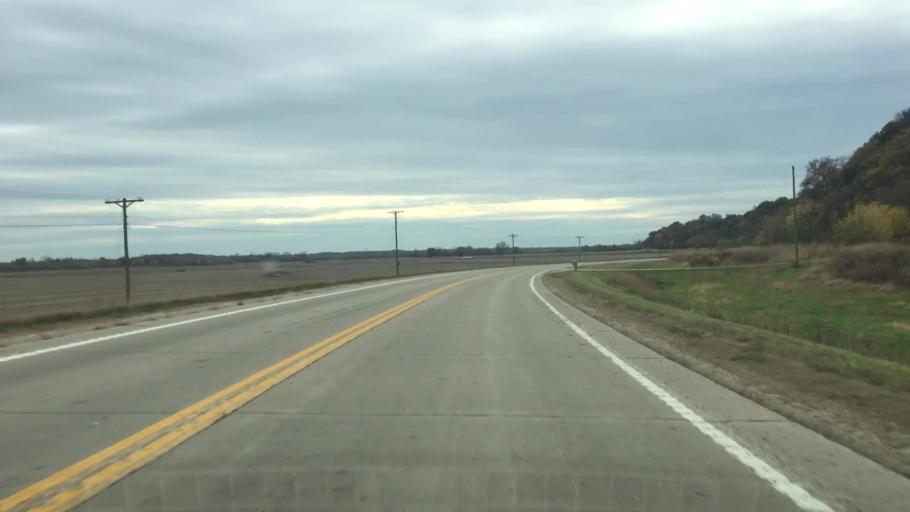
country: US
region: Missouri
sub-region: Callaway County
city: Holts Summit
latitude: 38.5876
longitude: -92.0306
